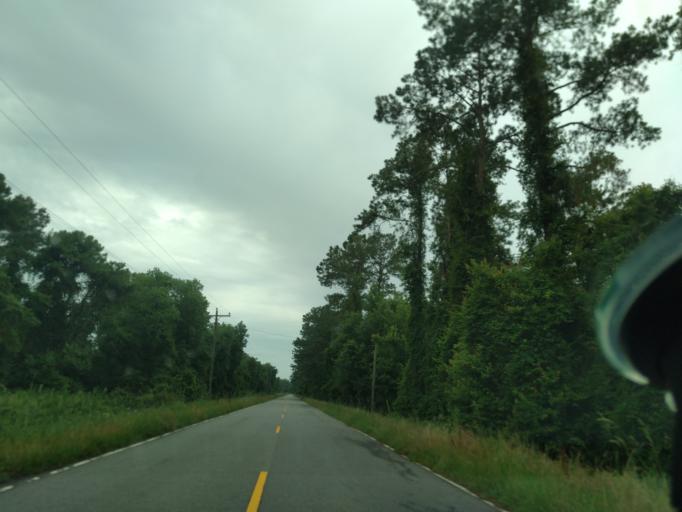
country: US
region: North Carolina
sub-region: Washington County
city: Plymouth
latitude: 35.7961
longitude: -76.5177
